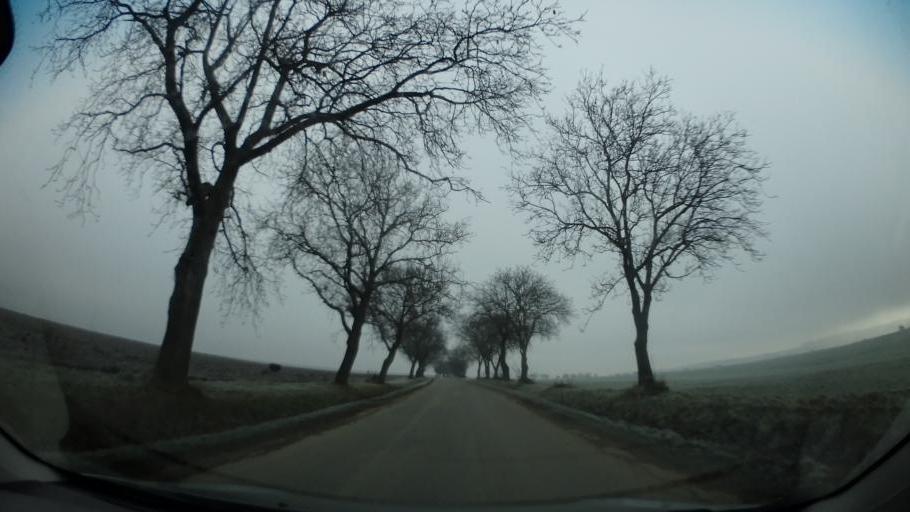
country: CZ
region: Vysocina
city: Mohelno
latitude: 49.1202
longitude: 16.2135
